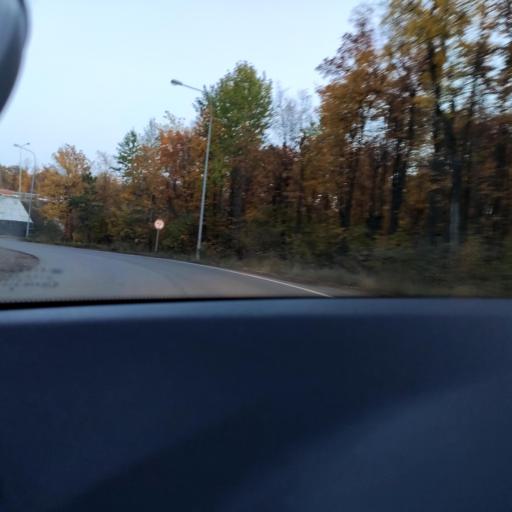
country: RU
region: Samara
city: Novosemeykino
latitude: 53.3816
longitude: 50.3120
